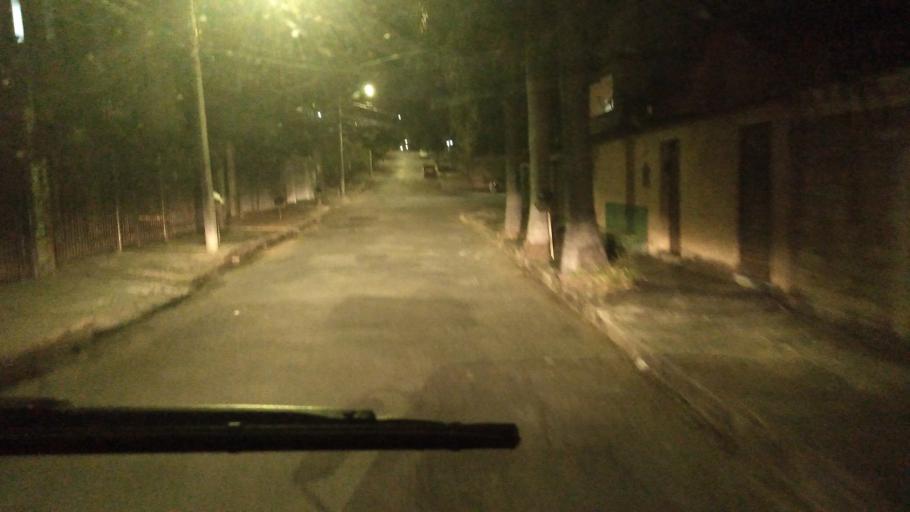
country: BR
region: Minas Gerais
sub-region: Belo Horizonte
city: Belo Horizonte
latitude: -19.8735
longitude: -43.9451
